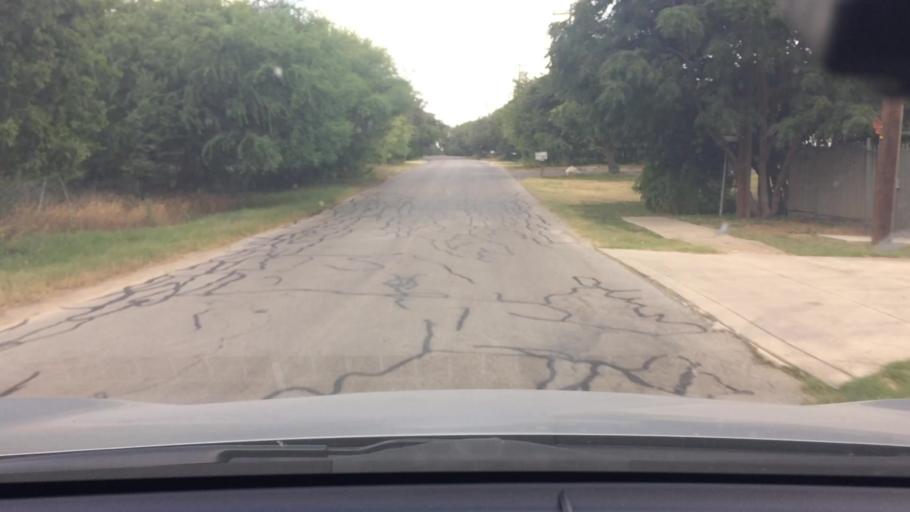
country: US
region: Texas
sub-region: Bexar County
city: Hollywood Park
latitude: 29.5555
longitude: -98.4673
